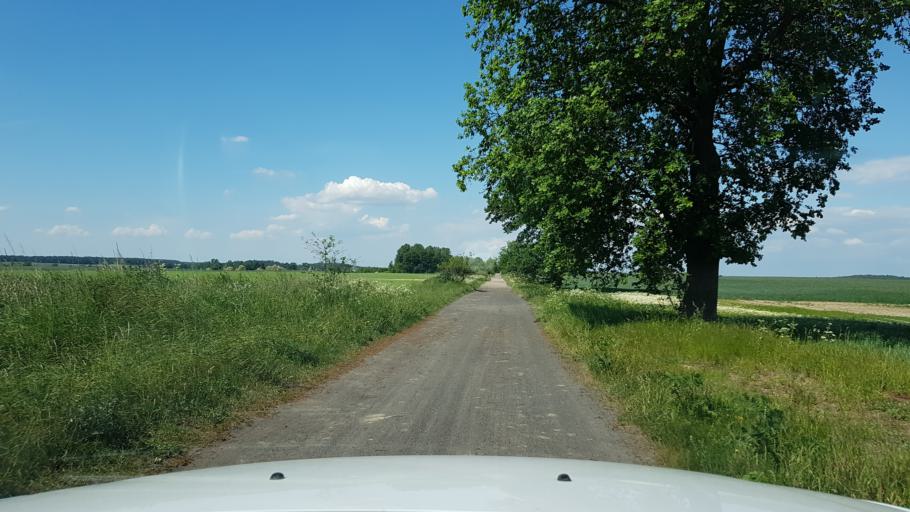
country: PL
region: West Pomeranian Voivodeship
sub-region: Powiat gryfinski
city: Banie
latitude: 53.1266
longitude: 14.5444
